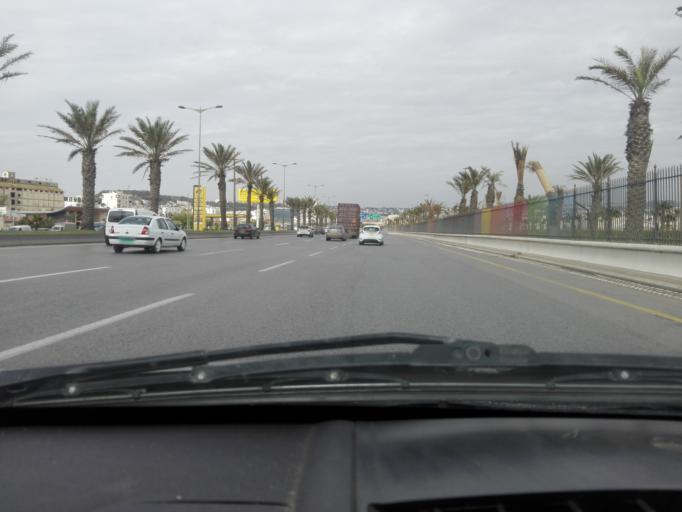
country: DZ
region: Alger
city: Algiers
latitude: 36.7461
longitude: 3.0985
